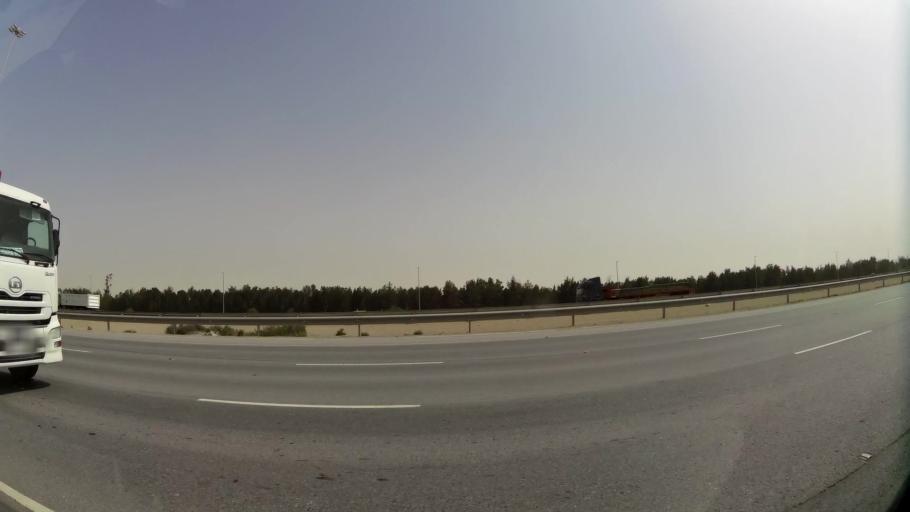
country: QA
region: Baladiyat ar Rayyan
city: Ar Rayyan
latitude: 25.1615
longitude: 51.2963
